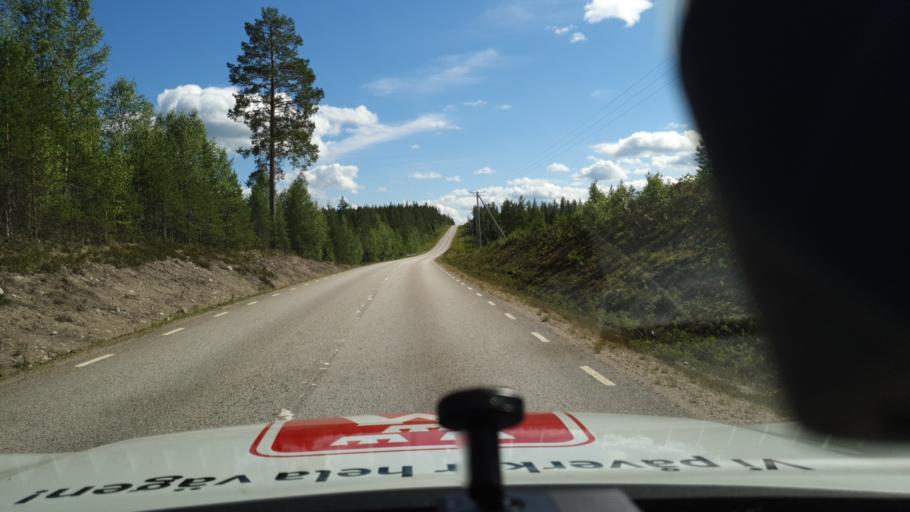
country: NO
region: Hedmark
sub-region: Trysil
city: Innbygda
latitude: 60.9909
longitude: 12.4925
